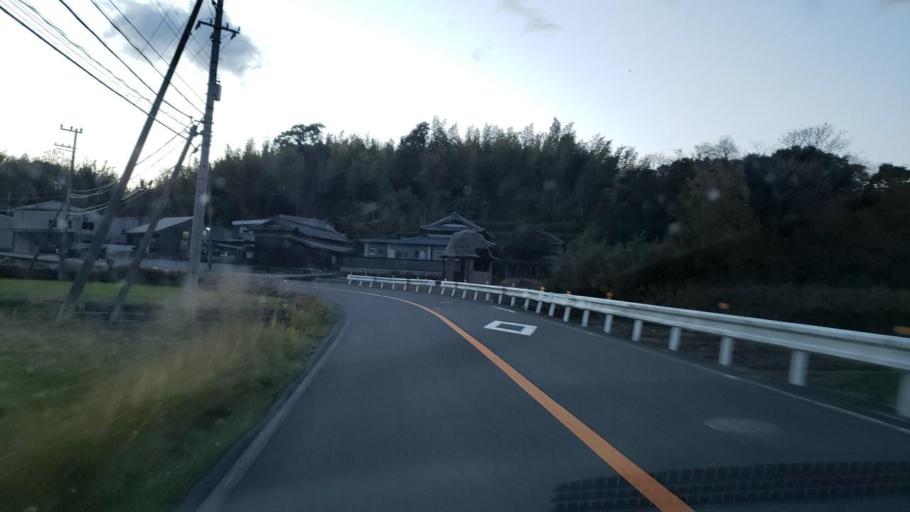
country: JP
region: Hyogo
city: Fukura
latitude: 34.2863
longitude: 134.6860
